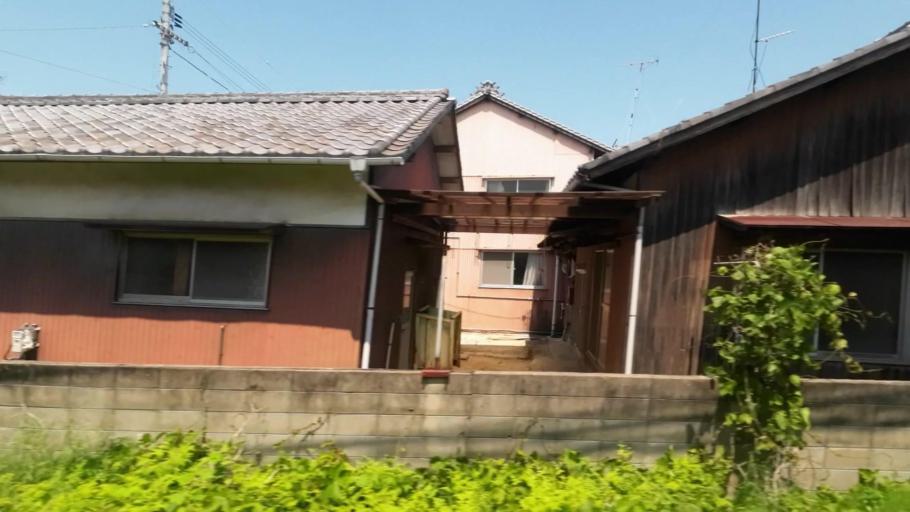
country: JP
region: Ehime
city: Hojo
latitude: 34.0351
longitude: 132.8445
